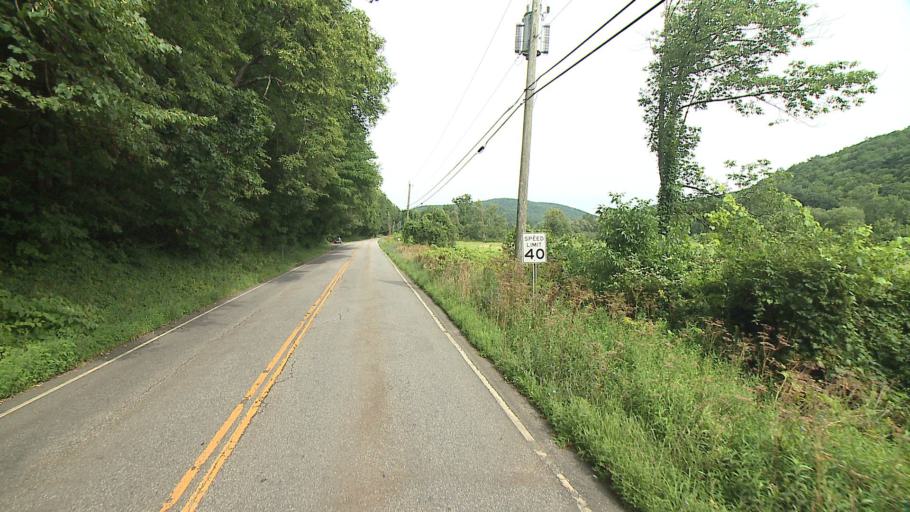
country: US
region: Connecticut
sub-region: Litchfield County
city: Kent
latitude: 41.7304
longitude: -73.4899
